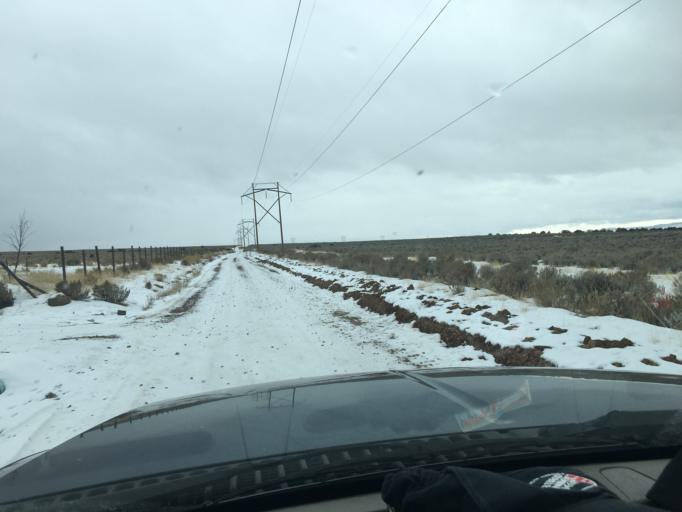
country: US
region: Colorado
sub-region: Garfield County
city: Parachute
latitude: 39.3414
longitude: -108.1702
